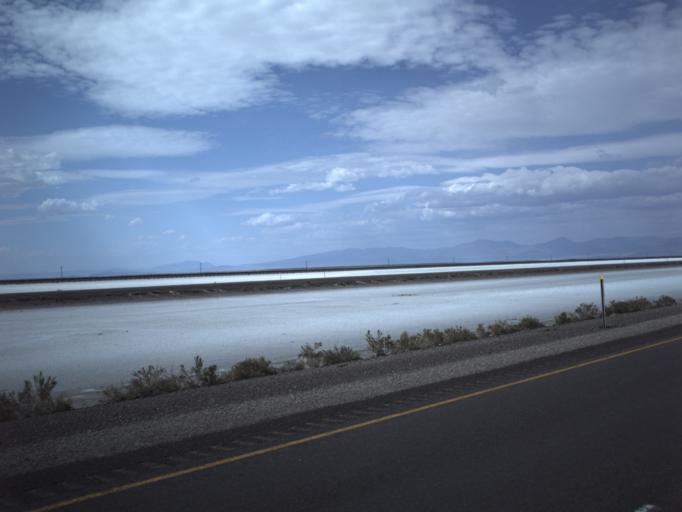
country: US
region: Utah
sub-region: Tooele County
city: Wendover
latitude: 40.7361
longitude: -113.6915
